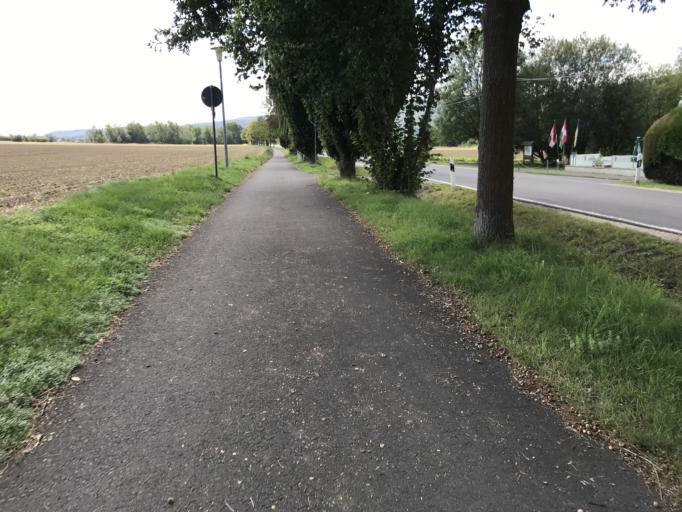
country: DE
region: Thuringia
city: Wahlhausen
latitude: 51.2887
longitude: 9.9774
